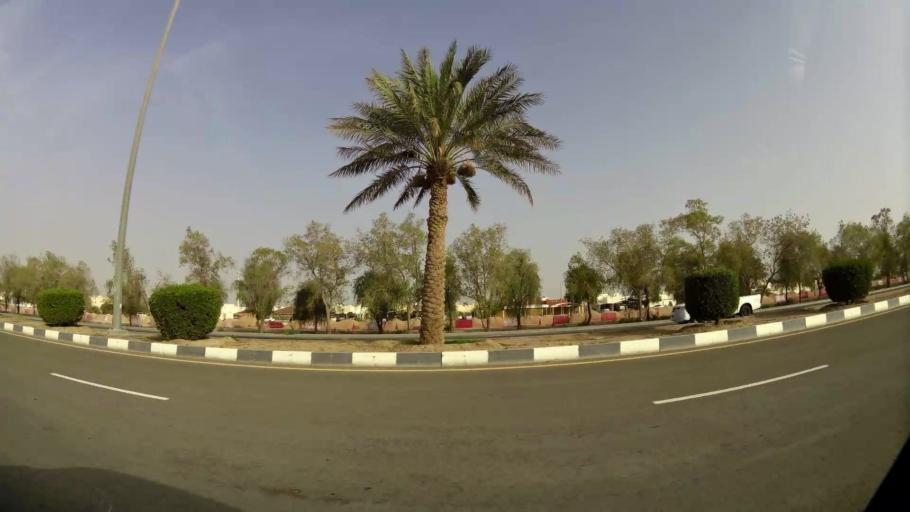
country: AE
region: Abu Dhabi
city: Al Ain
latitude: 24.1107
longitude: 55.6991
